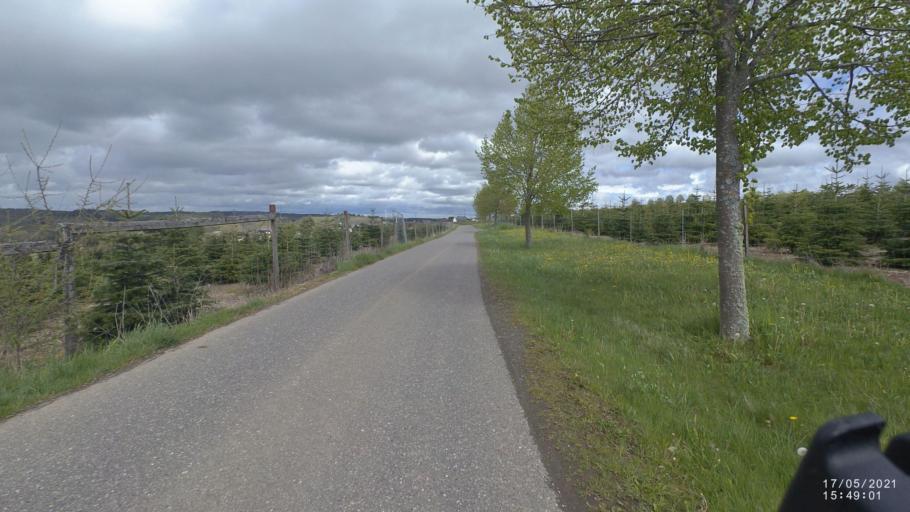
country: DE
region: Rheinland-Pfalz
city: Munk
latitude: 50.3049
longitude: 7.0340
